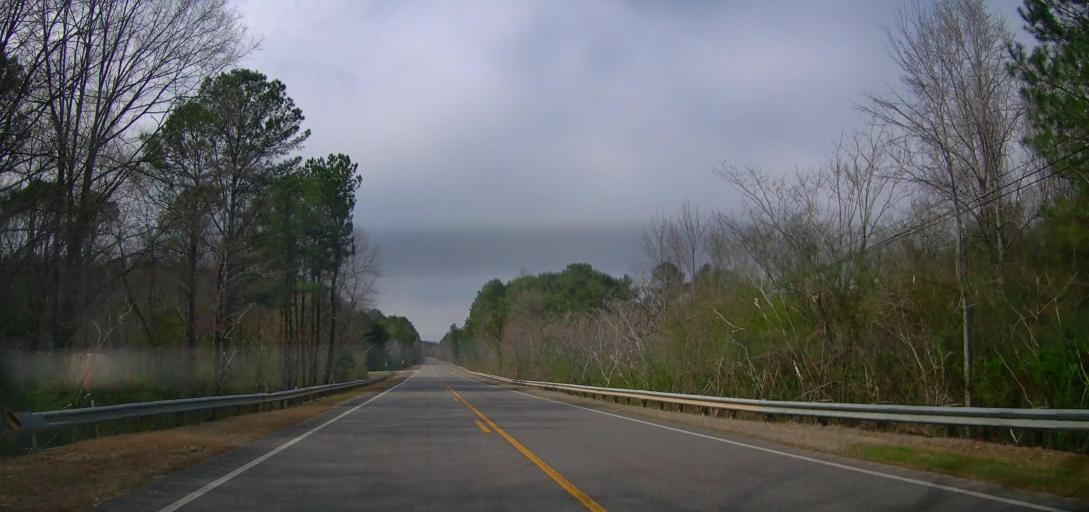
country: US
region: Alabama
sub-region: Walker County
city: Carbon Hill
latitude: 33.9085
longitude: -87.5560
